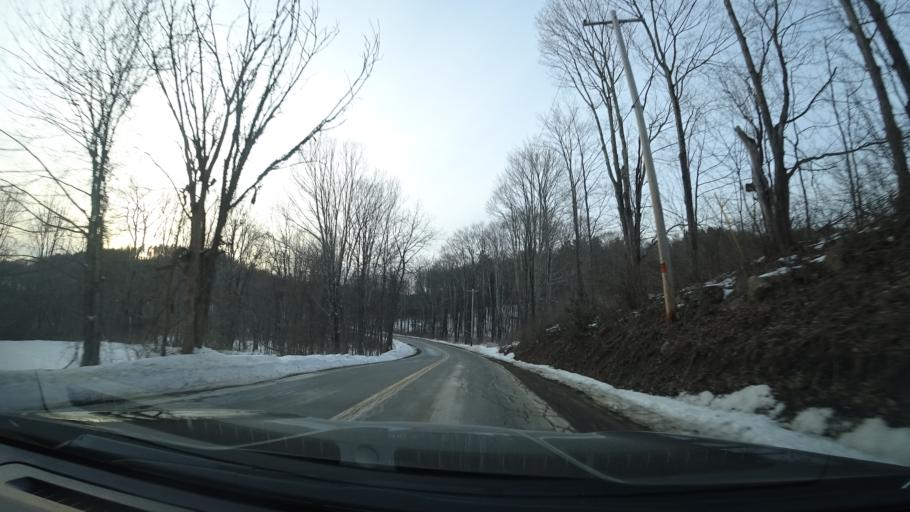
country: US
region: New York
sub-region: Washington County
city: Fort Edward
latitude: 43.2538
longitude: -73.4196
